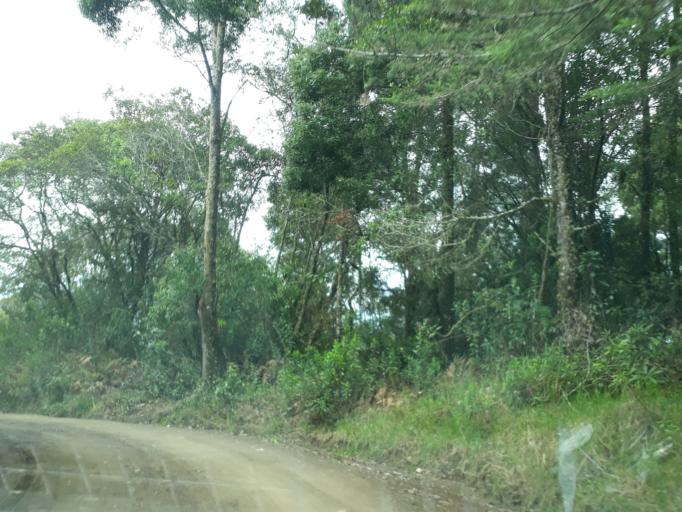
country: CO
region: Cundinamarca
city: Macheta
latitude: 5.1020
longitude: -73.5426
